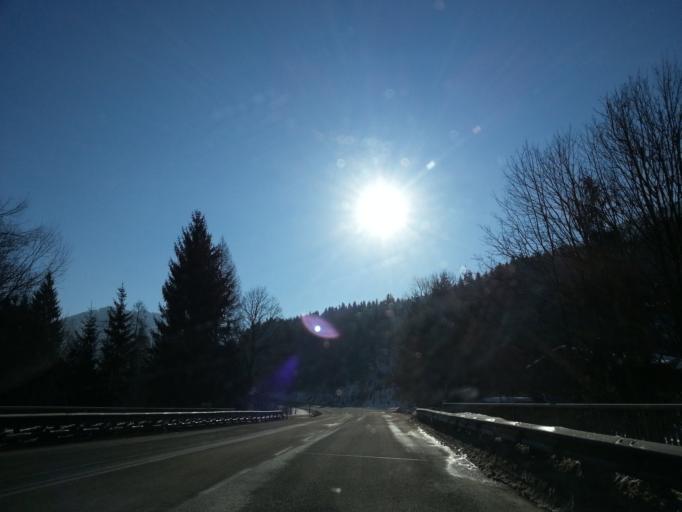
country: AT
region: Salzburg
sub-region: Politischer Bezirk Sankt Johann im Pongau
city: Eben im Pongau
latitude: 47.4197
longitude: 13.3714
